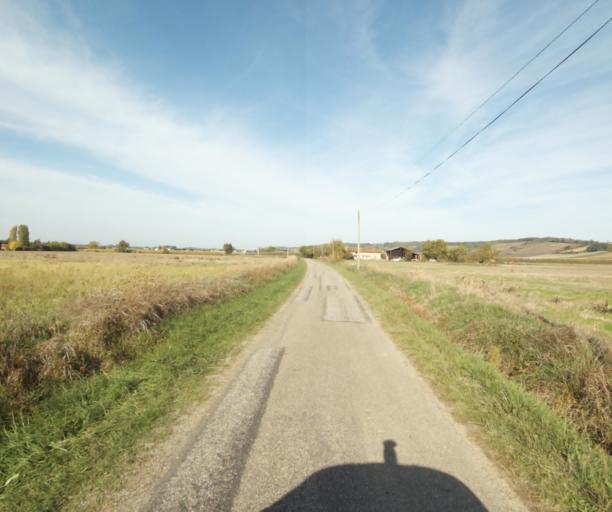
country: FR
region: Midi-Pyrenees
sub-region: Departement du Tarn-et-Garonne
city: Nohic
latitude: 43.9133
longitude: 1.4384
